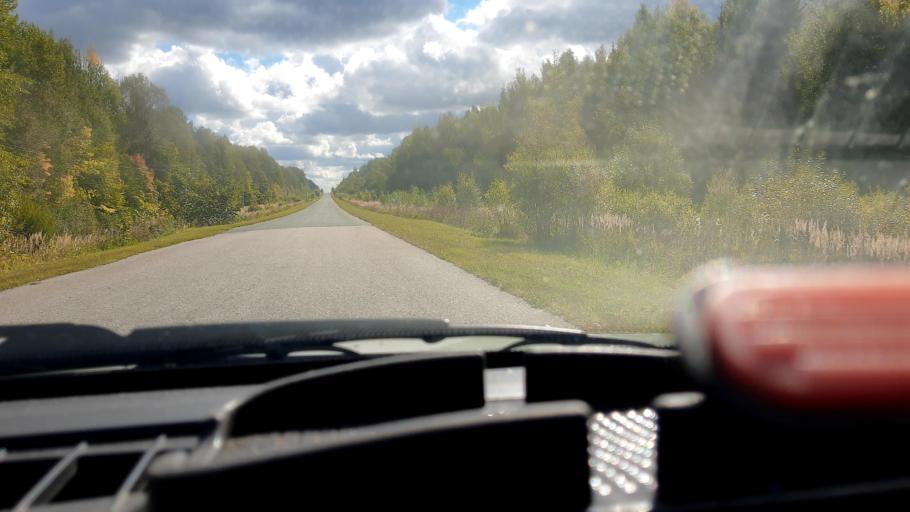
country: RU
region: Mariy-El
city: Kilemary
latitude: 56.9300
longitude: 46.7030
